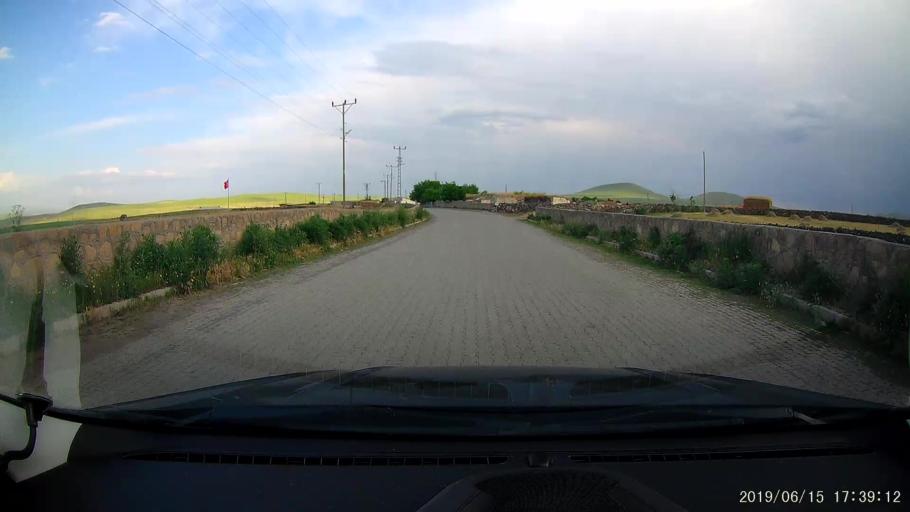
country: TR
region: Kars
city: Basgedikler
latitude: 40.5172
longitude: 43.5694
